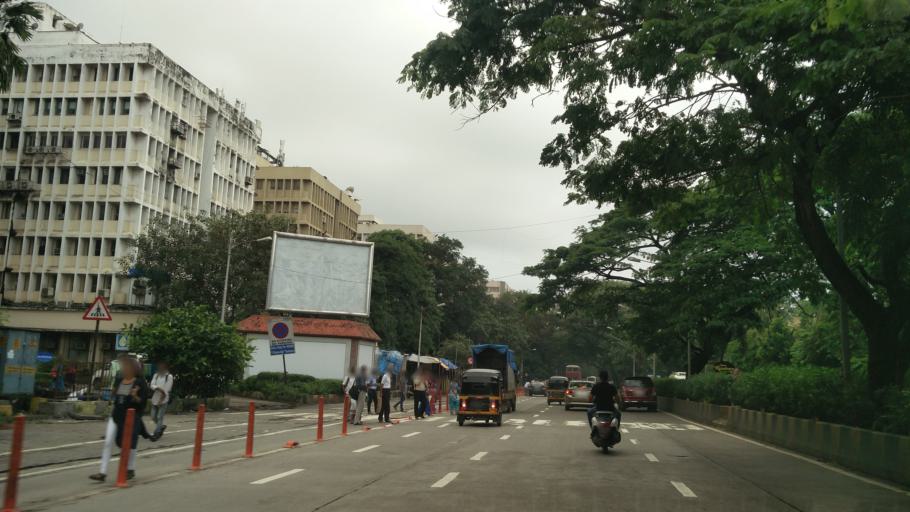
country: IN
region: Maharashtra
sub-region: Mumbai Suburban
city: Mumbai
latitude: 19.0573
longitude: 72.8528
